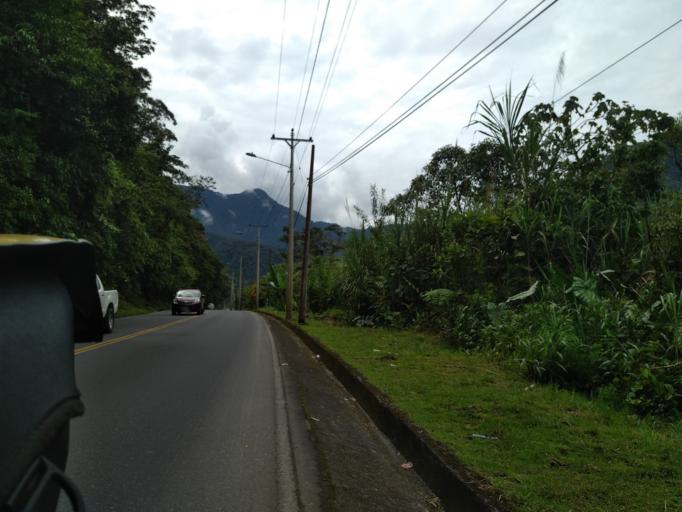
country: EC
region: Pastaza
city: Puyo
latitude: -1.4122
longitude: -78.2010
